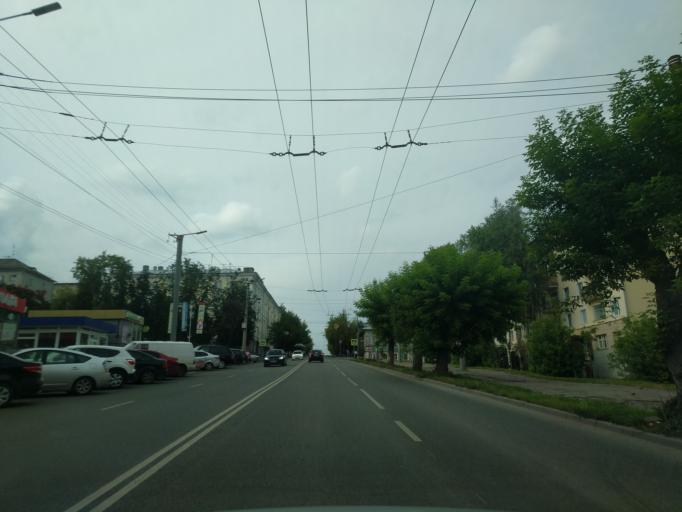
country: RU
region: Kirov
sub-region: Kirovo-Chepetskiy Rayon
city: Kirov
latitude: 58.5907
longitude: 49.6691
